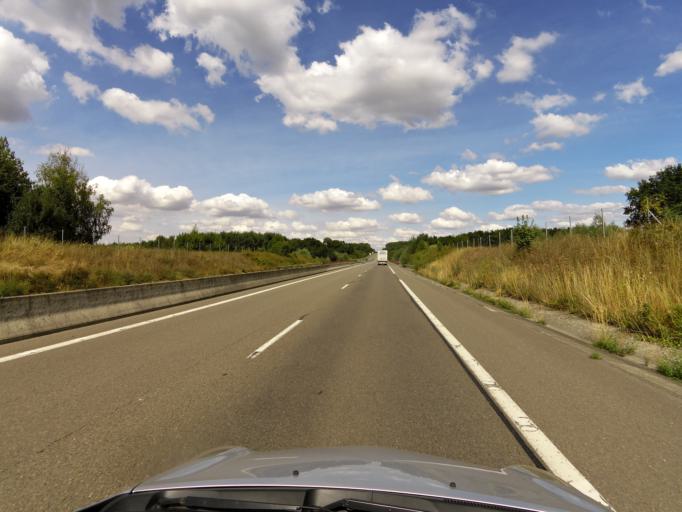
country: FR
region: Picardie
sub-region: Departement de l'Aisne
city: Vailly-sur-Aisne
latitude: 49.4825
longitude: 3.5399
